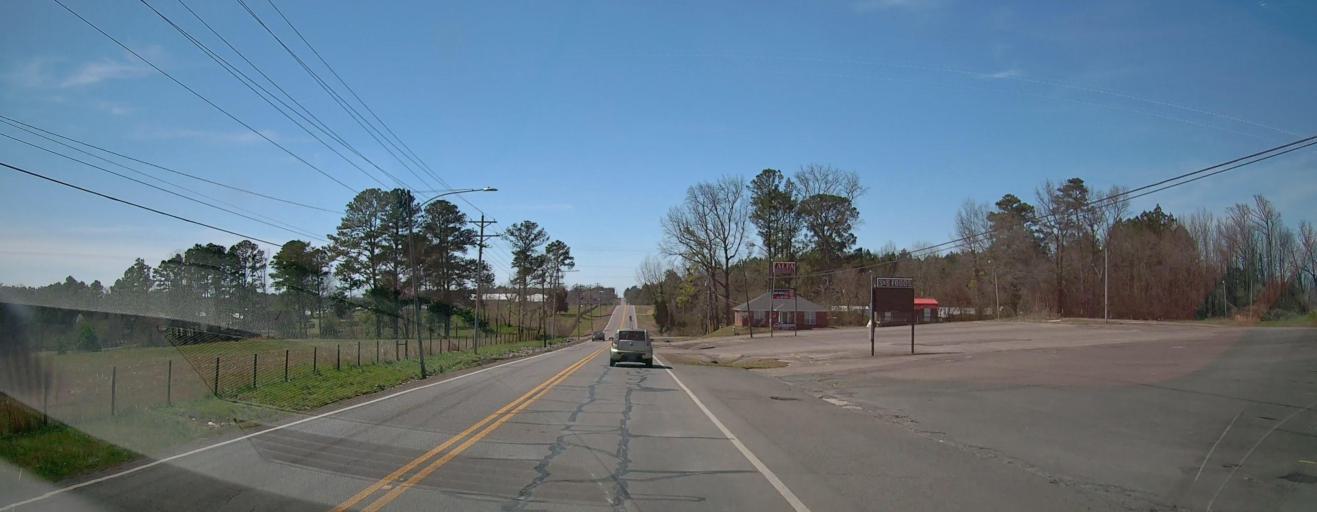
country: US
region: Alabama
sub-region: Blount County
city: Blountsville
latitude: 34.1744
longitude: -86.6189
